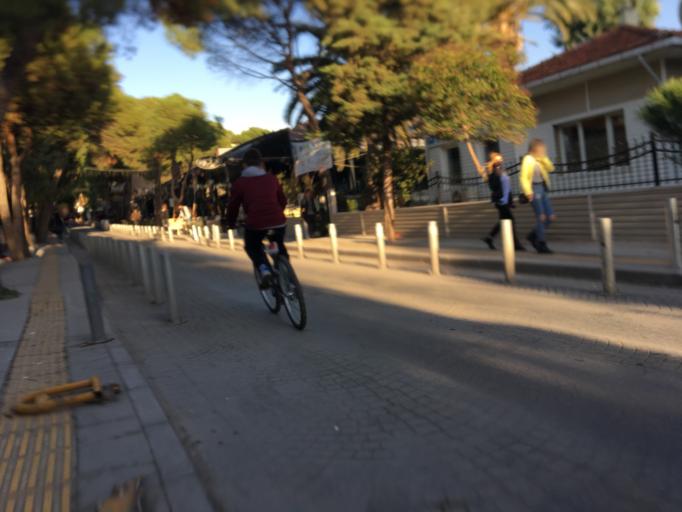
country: TR
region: Izmir
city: Buca
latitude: 38.3877
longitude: 27.1645
